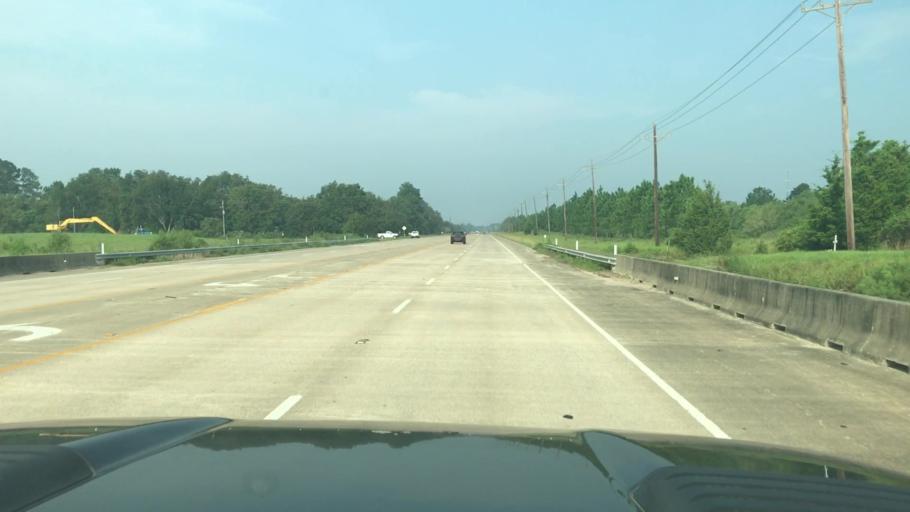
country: US
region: Texas
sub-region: Jefferson County
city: Bevil Oaks
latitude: 30.1331
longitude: -94.2234
